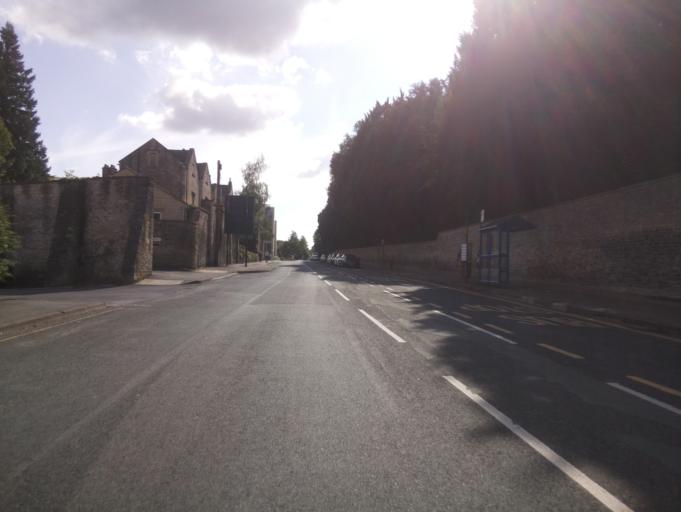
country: GB
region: England
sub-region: Gloucestershire
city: Cirencester
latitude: 51.7157
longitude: -1.9720
